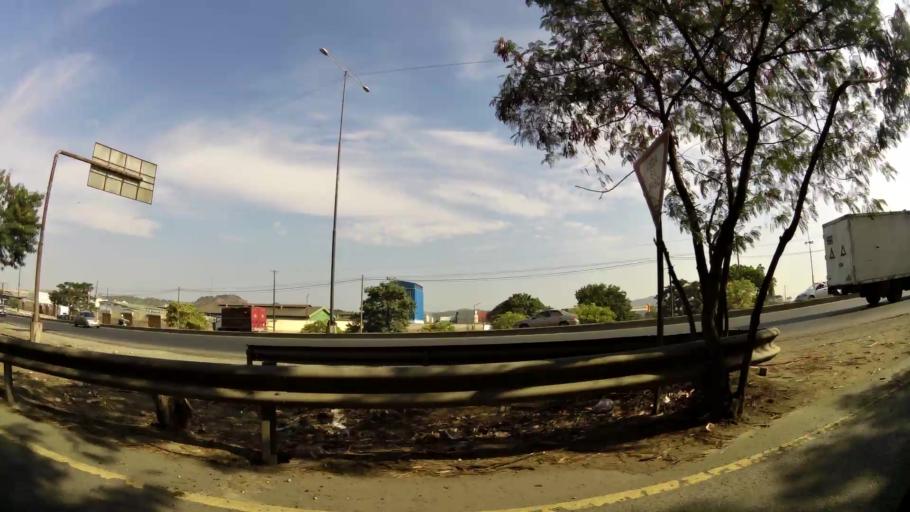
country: EC
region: Guayas
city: Santa Lucia
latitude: -2.0830
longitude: -79.9404
